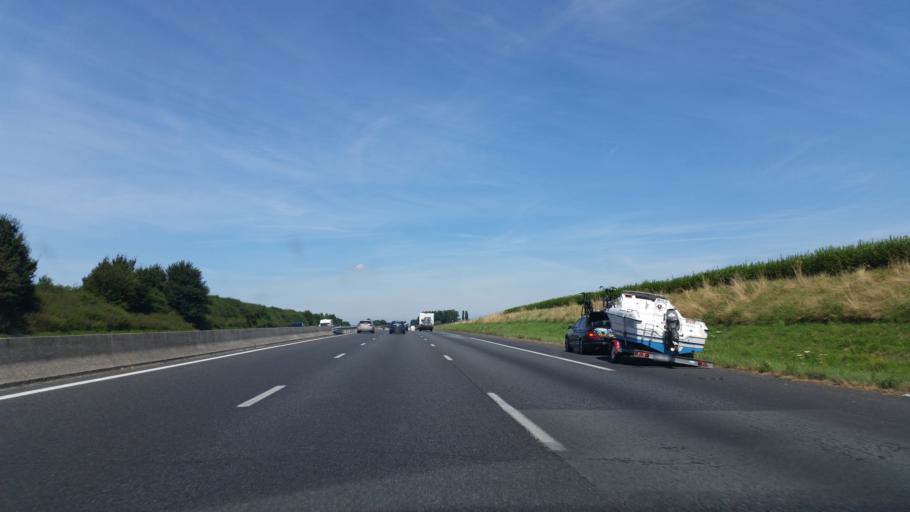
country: FR
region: Nord-Pas-de-Calais
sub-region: Departement du Pas-de-Calais
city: Vaulx-Vraucourt
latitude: 50.1400
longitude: 2.8723
